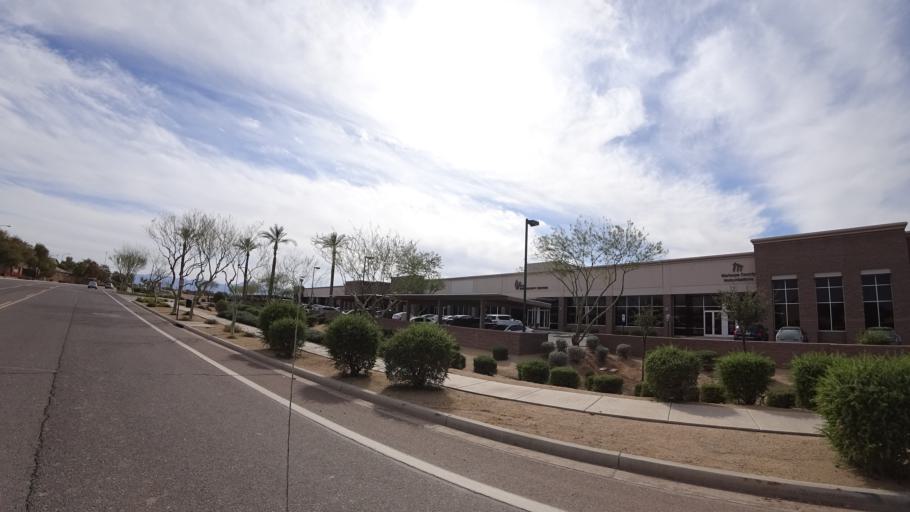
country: US
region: Arizona
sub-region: Maricopa County
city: Tolleson
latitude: 33.4681
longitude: -112.2644
